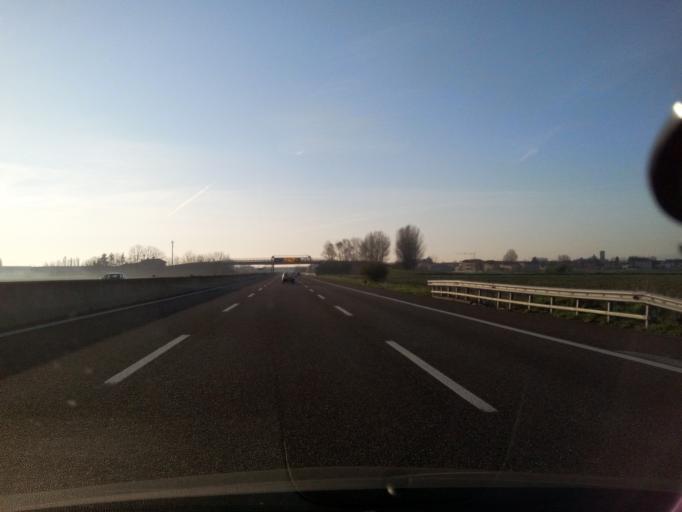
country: IT
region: Lombardy
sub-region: Provincia di Lodi
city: Guardamiglio
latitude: 45.1184
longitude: 9.6756
